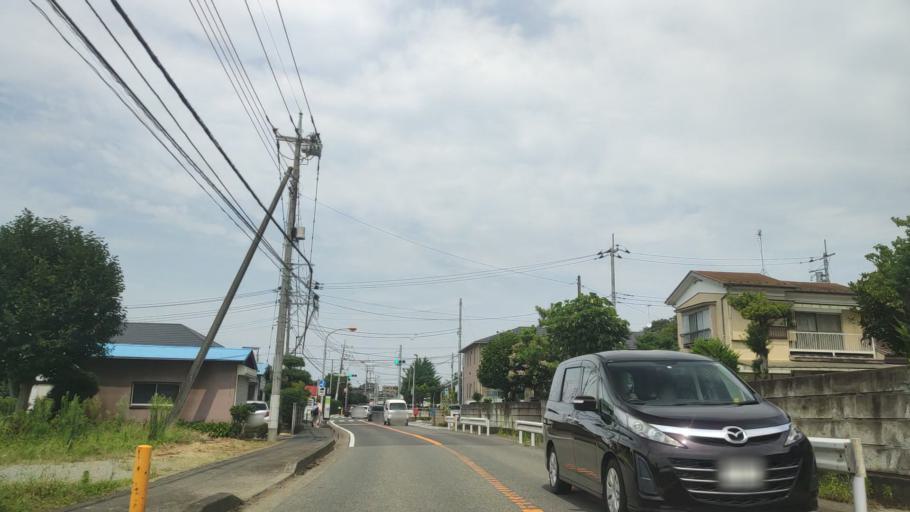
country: JP
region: Kanagawa
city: Atsugi
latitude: 35.4379
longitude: 139.3942
